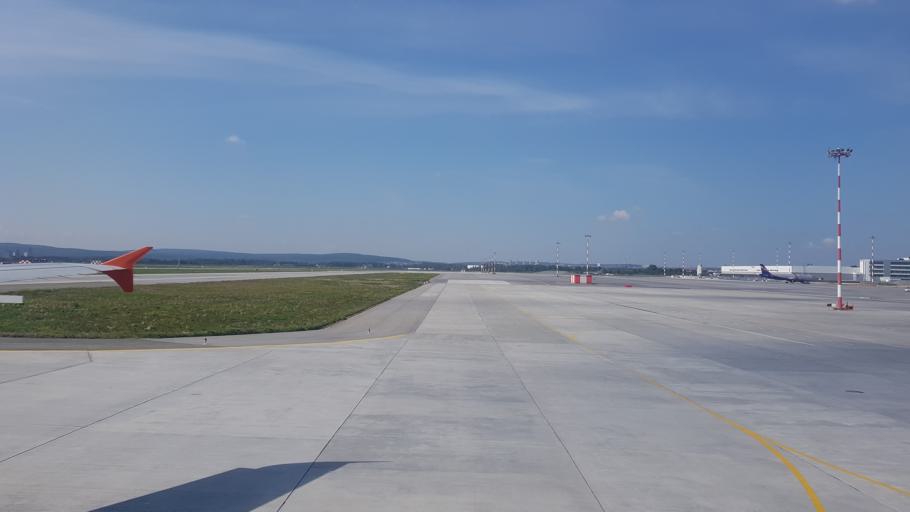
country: RU
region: Sverdlovsk
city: Istok
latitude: 56.7469
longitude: 60.8013
